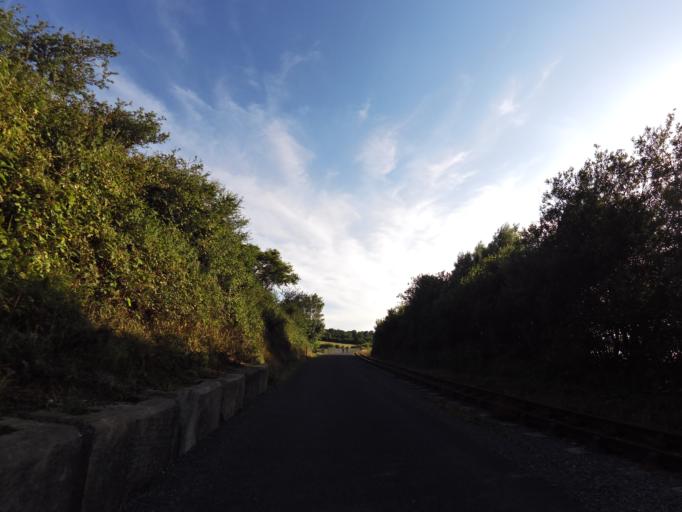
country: IE
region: Leinster
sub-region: Kilkenny
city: Mooncoin
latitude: 52.2484
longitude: -7.1973
